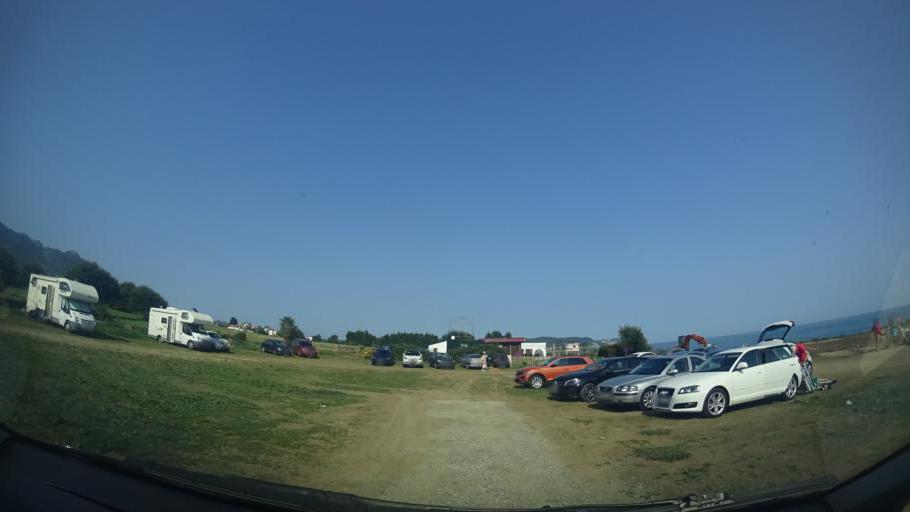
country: ES
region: Asturias
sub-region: Province of Asturias
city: Colunga
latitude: 43.4731
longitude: -5.2042
